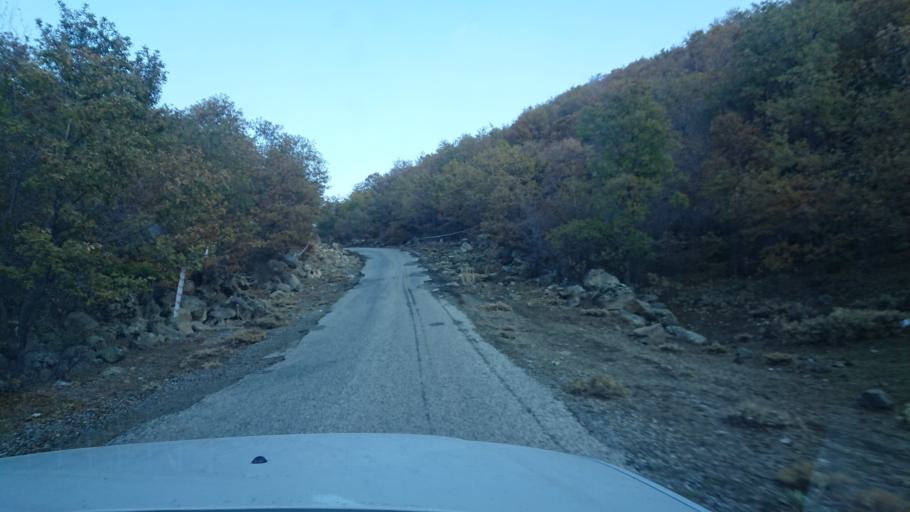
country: TR
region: Aksaray
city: Taspinar
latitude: 38.1658
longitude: 34.1969
